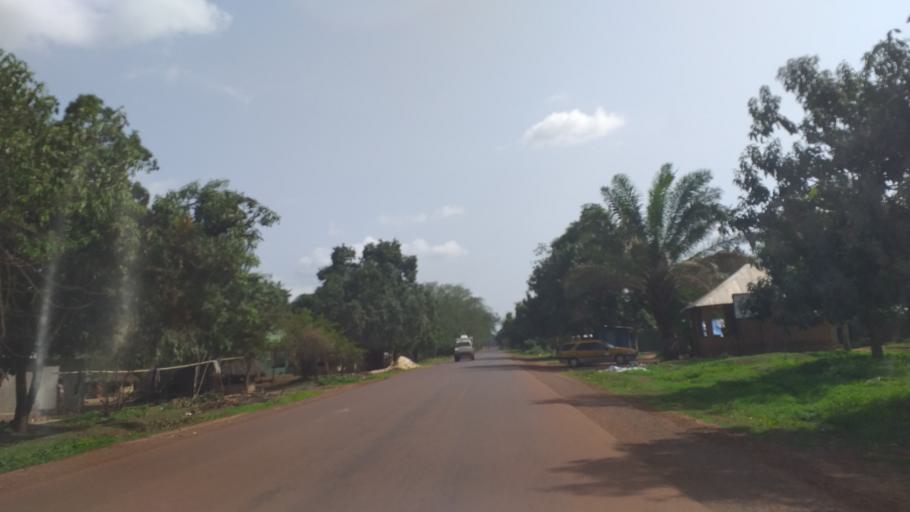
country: GN
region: Boke
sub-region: Boke Prefecture
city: Sangueya
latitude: 10.8206
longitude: -14.3749
